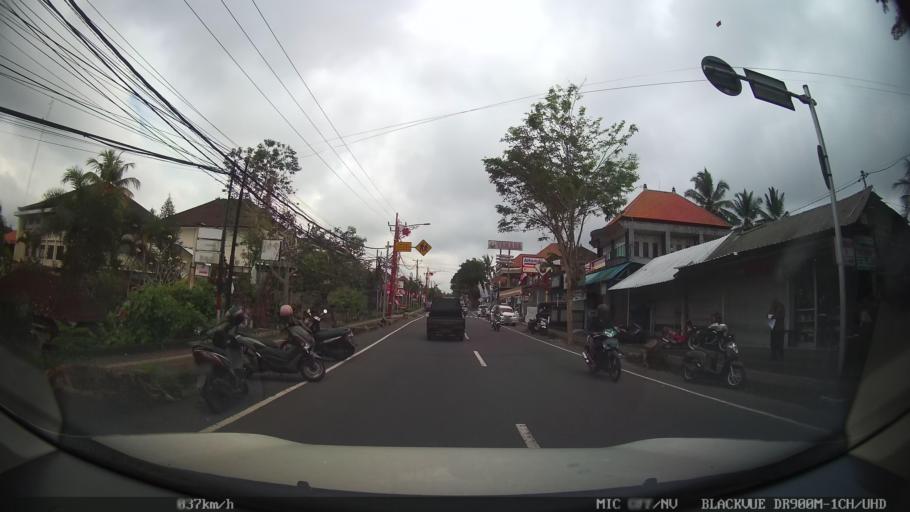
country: ID
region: Bali
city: Bangli
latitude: -8.4588
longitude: 115.3528
